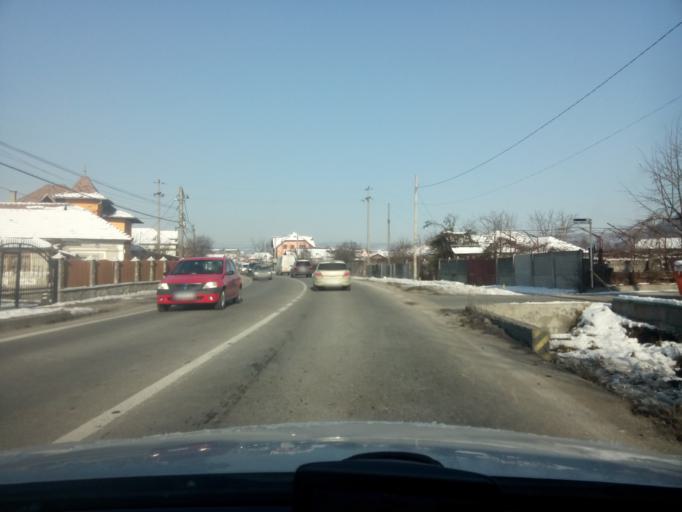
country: RO
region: Valcea
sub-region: Municipiul Ramnicu Valcea
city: Goranu
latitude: 45.0984
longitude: 24.3822
